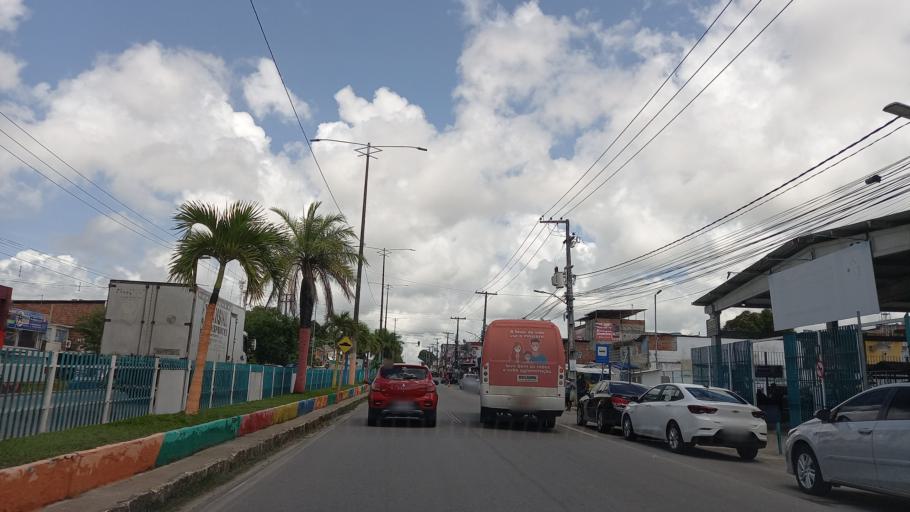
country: BR
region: Pernambuco
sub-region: Jaboatao Dos Guararapes
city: Jaboatao
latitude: -8.2358
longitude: -34.9809
